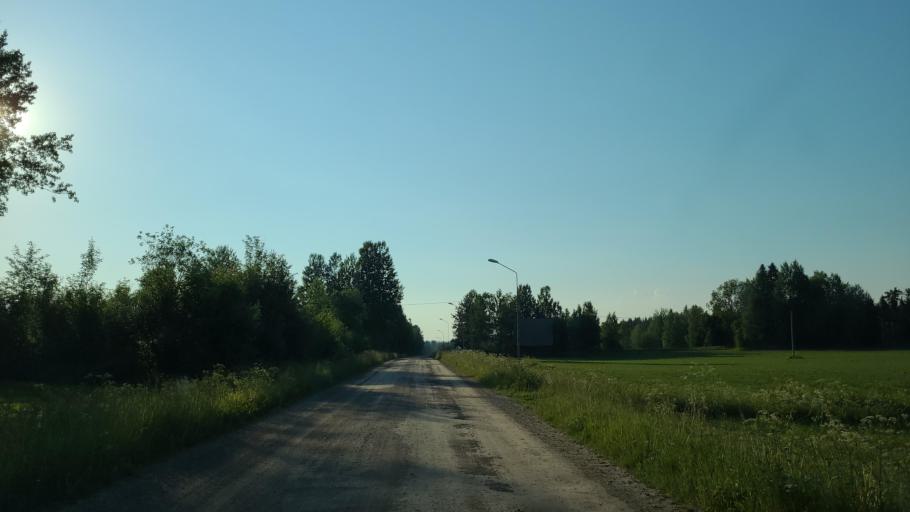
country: SE
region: Vaesterbotten
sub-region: Skelleftea Kommun
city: Burea
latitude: 64.4007
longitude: 21.3718
